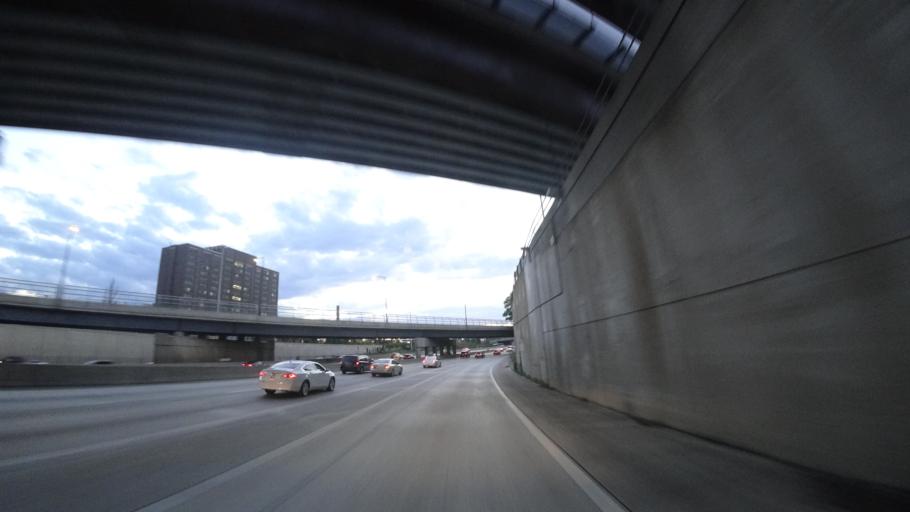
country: US
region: Illinois
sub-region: Cook County
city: Chicago
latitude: 41.7773
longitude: -87.6292
